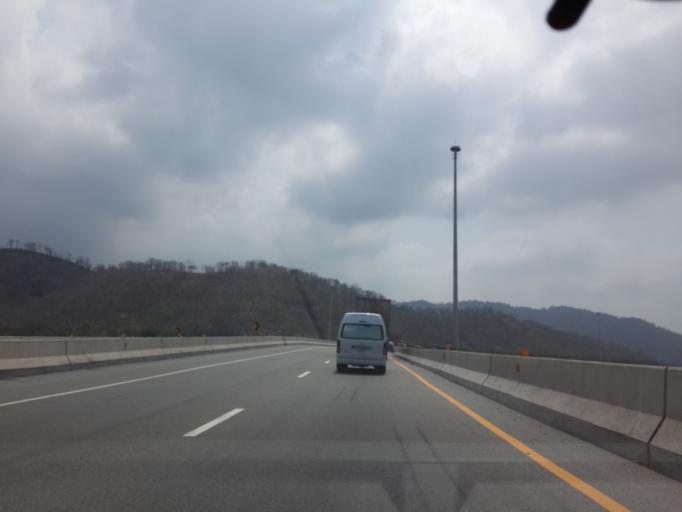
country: TH
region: Chon Buri
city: Chon Buri
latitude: 13.3025
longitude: 100.9947
